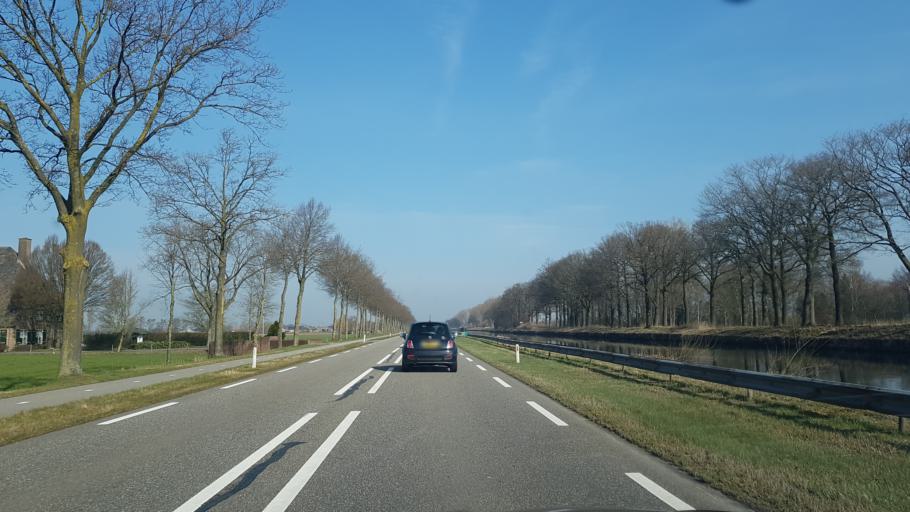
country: NL
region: Limburg
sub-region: Gemeente Nederweert
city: Nederweert
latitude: 51.3174
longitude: 5.7486
